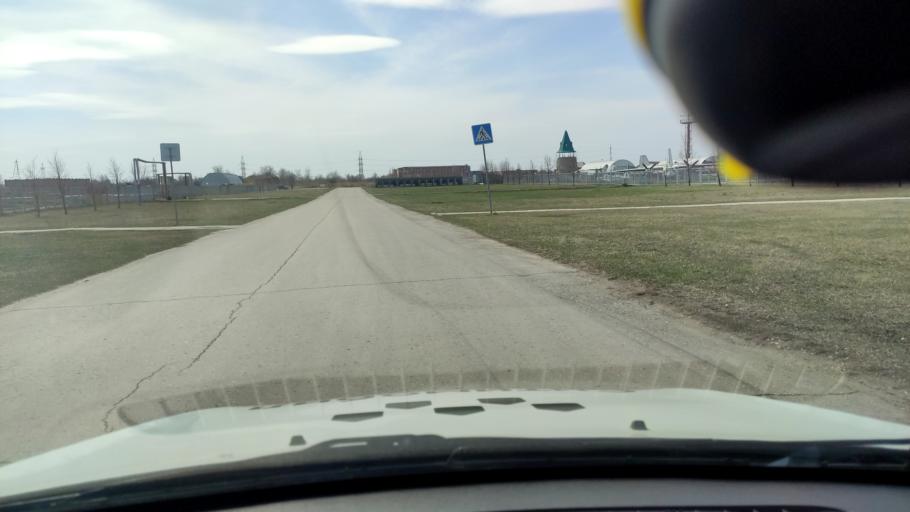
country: RU
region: Samara
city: Tol'yatti
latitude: 53.5532
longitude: 49.2528
